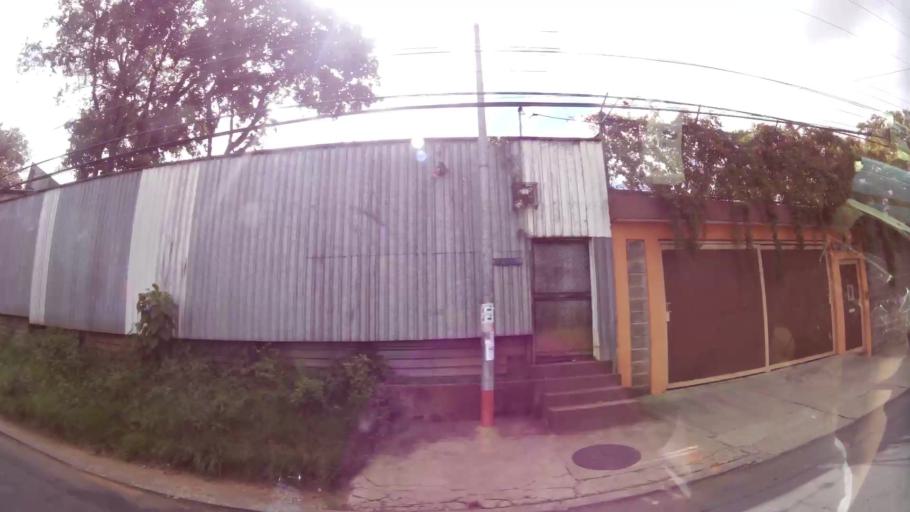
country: GT
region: Guatemala
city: Guatemala City
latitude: 14.6820
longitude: -90.5509
